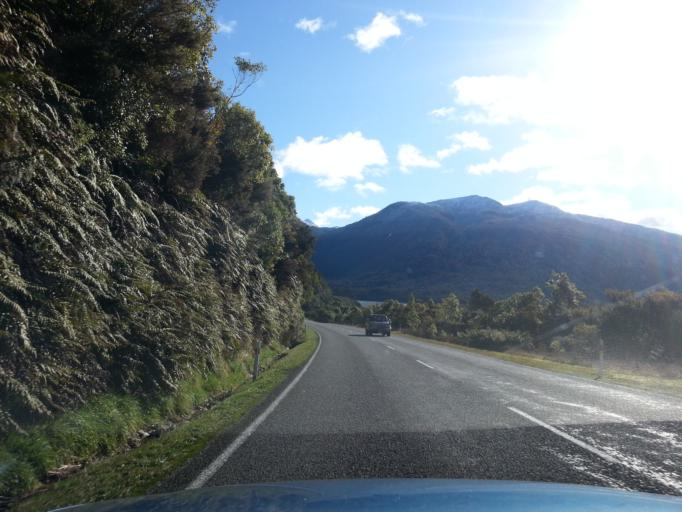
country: NZ
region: West Coast
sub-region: Grey District
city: Greymouth
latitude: -42.7371
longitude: 171.4565
